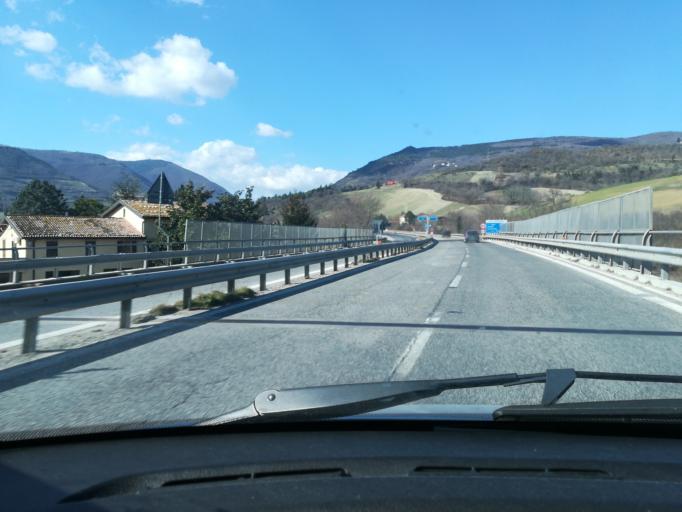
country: IT
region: The Marches
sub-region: Provincia di Macerata
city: Caldarola
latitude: 43.1515
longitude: 13.2205
